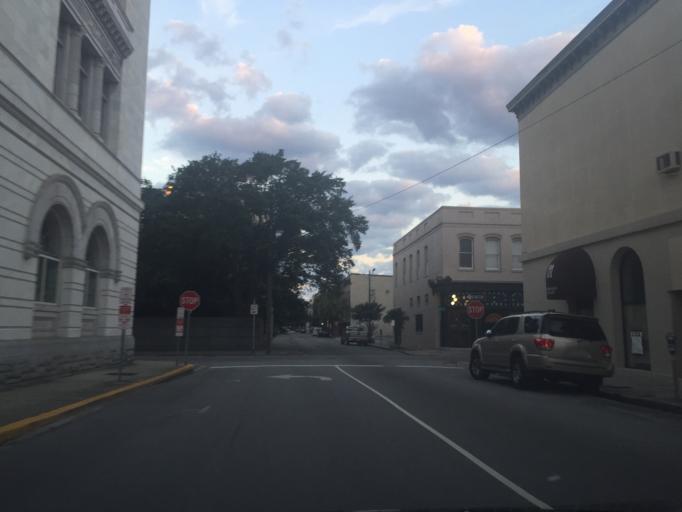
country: US
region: Georgia
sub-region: Chatham County
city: Savannah
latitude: 32.0784
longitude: -81.0930
